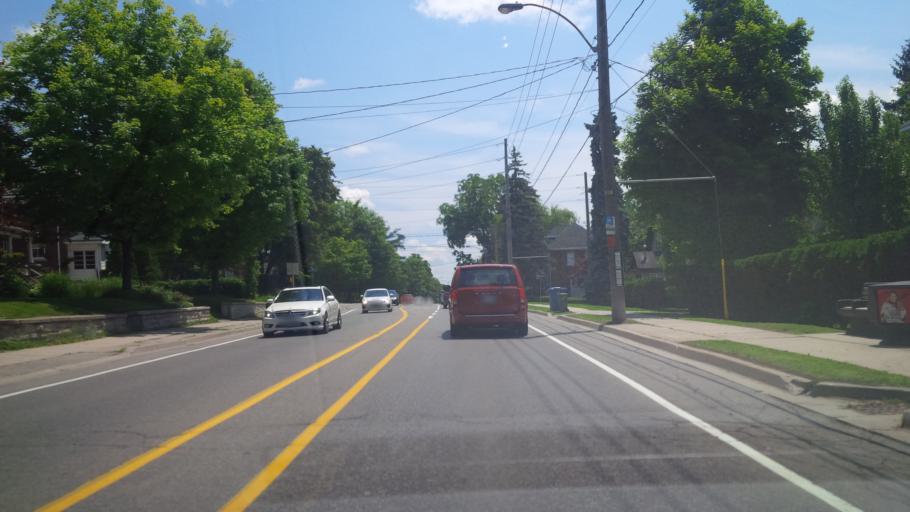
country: CA
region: Ontario
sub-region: Wellington County
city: Guelph
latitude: 43.5343
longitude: -80.2356
